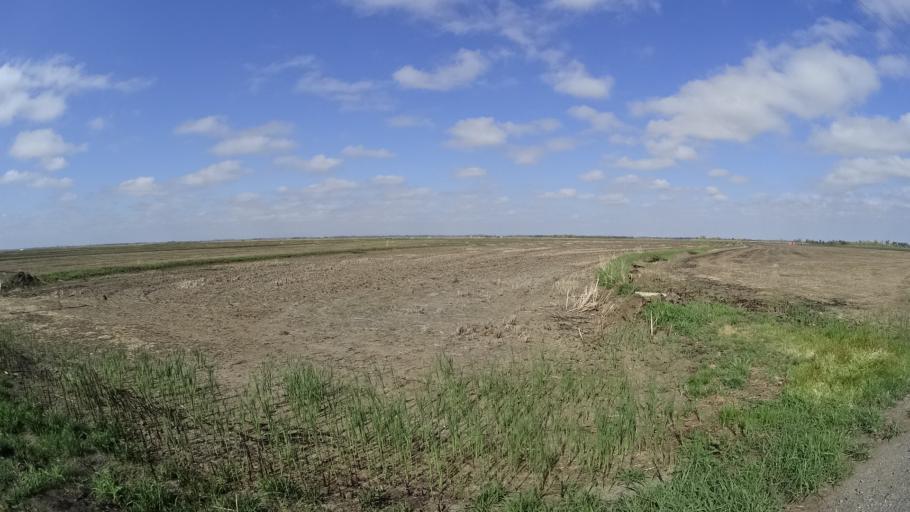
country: US
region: California
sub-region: Colusa County
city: Colusa
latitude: 39.3803
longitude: -121.9363
